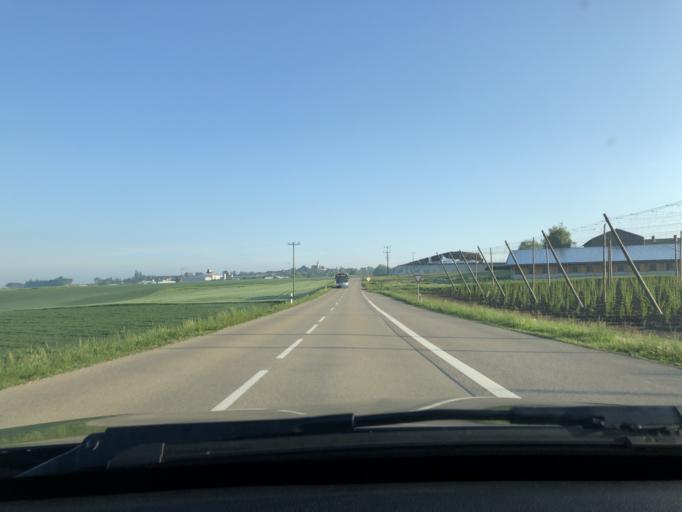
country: DE
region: Bavaria
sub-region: Upper Bavaria
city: Schweitenkirchen
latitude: 48.4942
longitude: 11.6138
